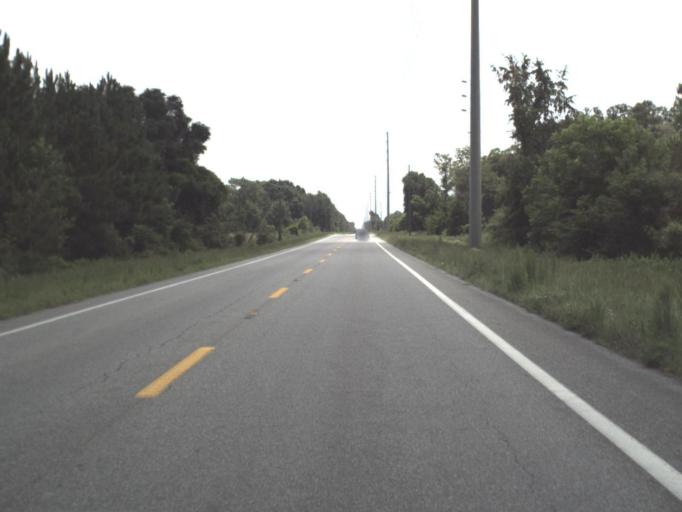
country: US
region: Florida
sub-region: Madison County
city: Madison
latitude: 30.4138
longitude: -83.2781
